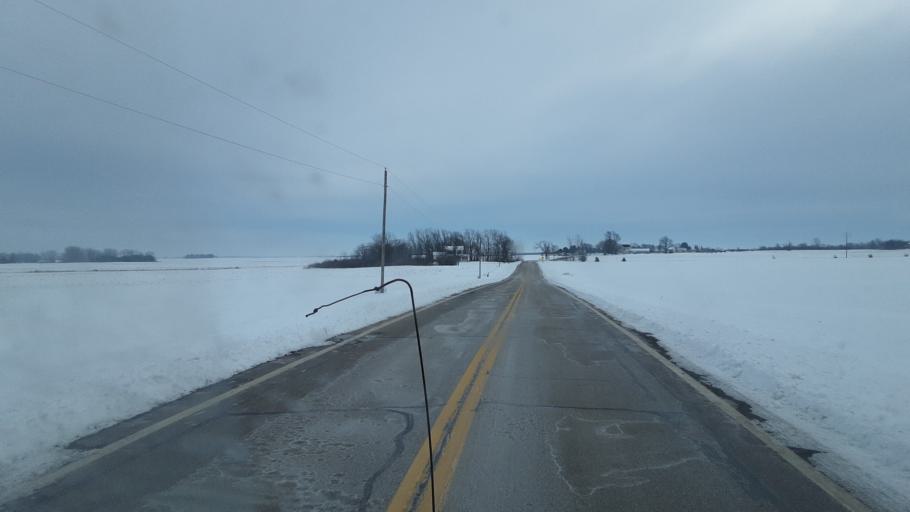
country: US
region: Ohio
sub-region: Champaign County
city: Mechanicsburg
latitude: 40.0223
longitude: -83.5184
